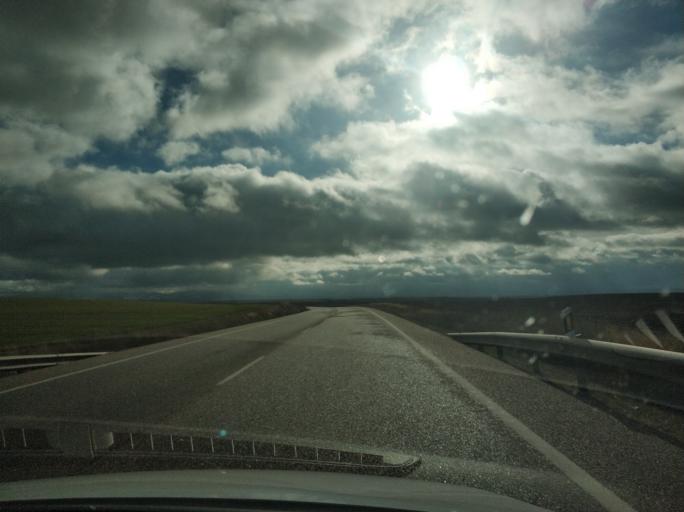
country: ES
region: Castille and Leon
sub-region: Provincia de Segovia
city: Ayllon
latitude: 41.4504
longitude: -3.3406
